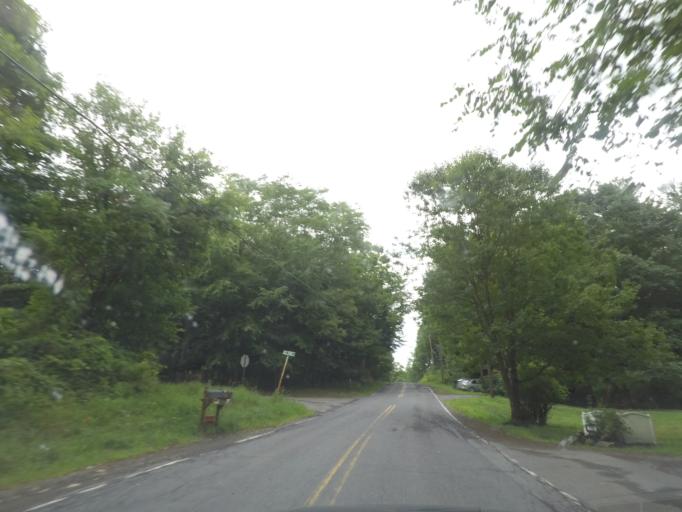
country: US
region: New York
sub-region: Rensselaer County
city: West Sand Lake
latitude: 42.6740
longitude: -73.6084
